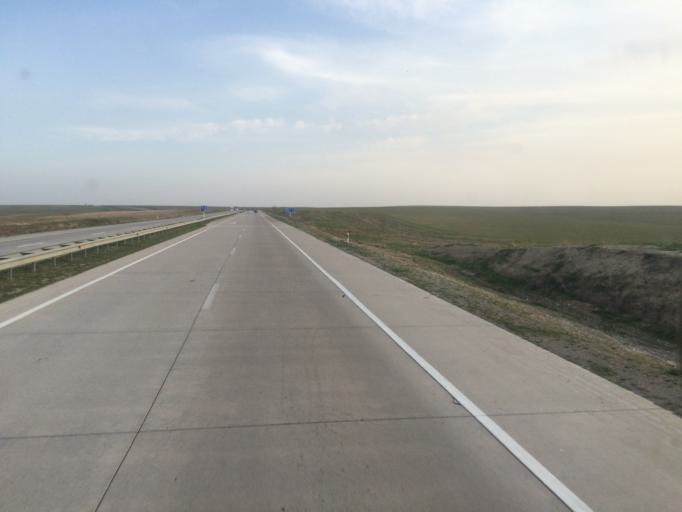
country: KZ
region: Ongtustik Qazaqstan
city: Temirlanovka
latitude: 42.6938
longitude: 69.2100
